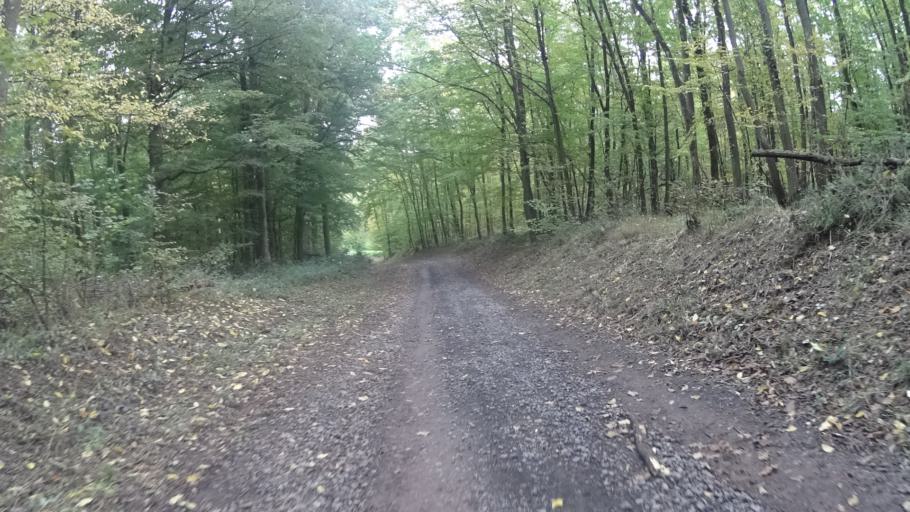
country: DE
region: Rheinland-Pfalz
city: Bolanden
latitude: 49.6338
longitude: 7.9979
